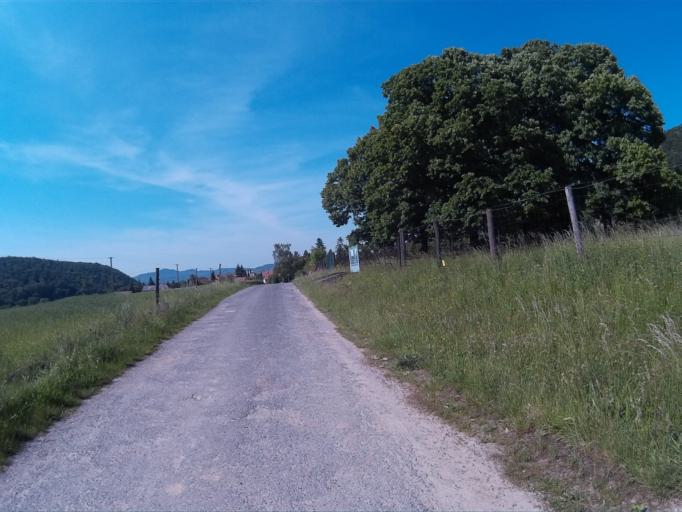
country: HU
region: Zala
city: Gyenesdias
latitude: 46.8398
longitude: 17.3044
